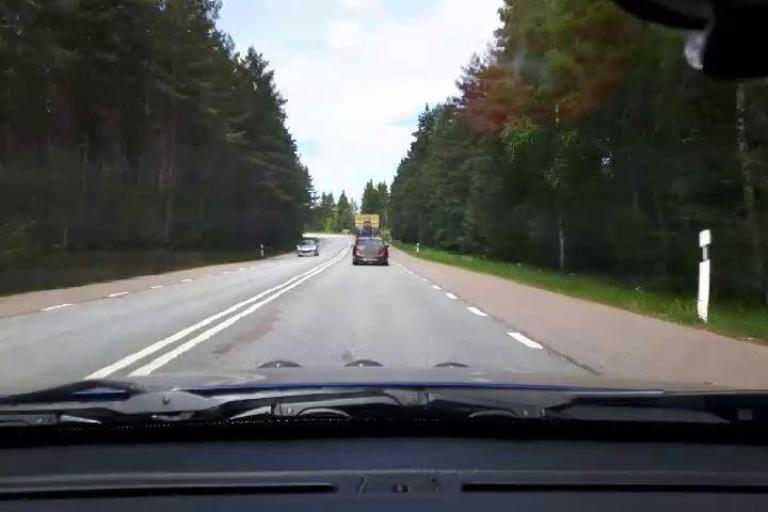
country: SE
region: Uppsala
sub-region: Osthammars Kommun
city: Bjorklinge
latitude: 60.0453
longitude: 17.5506
